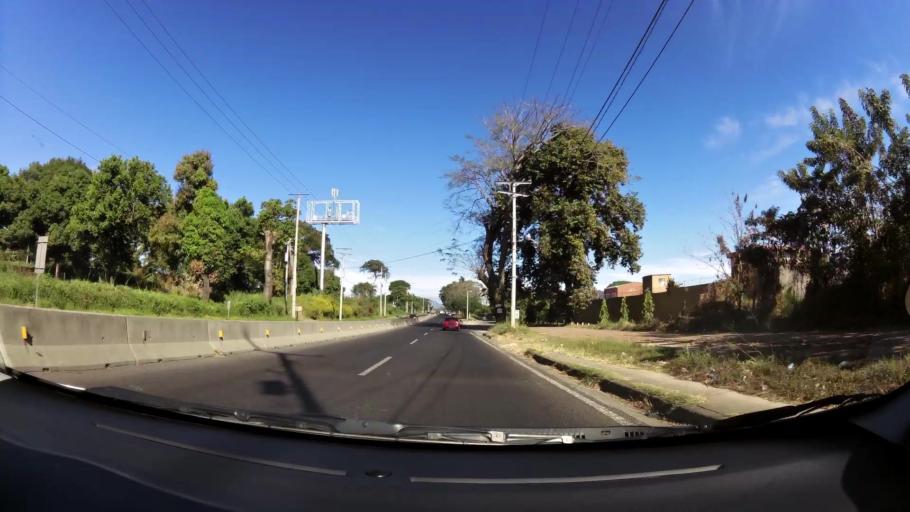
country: SV
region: Santa Ana
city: Santa Ana
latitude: 13.9598
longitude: -89.5780
